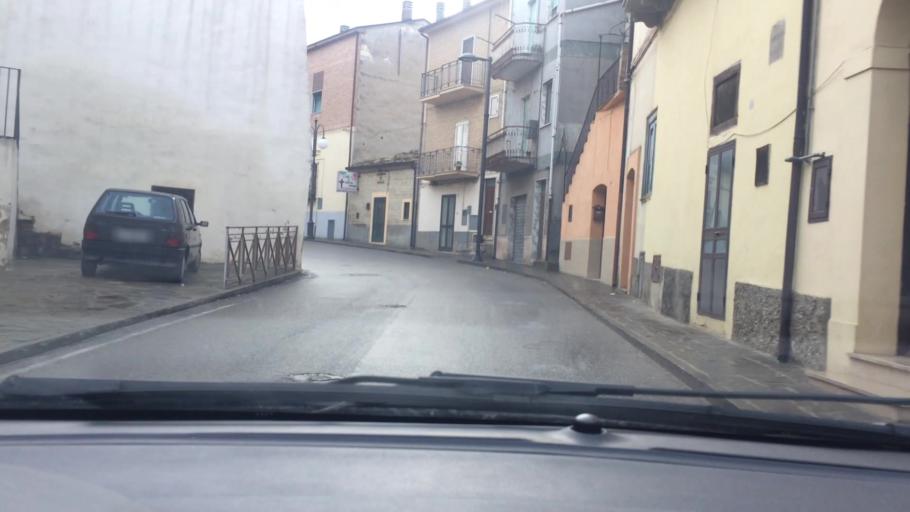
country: IT
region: Basilicate
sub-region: Provincia di Matera
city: San Mauro Forte
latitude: 40.4865
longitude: 16.2483
